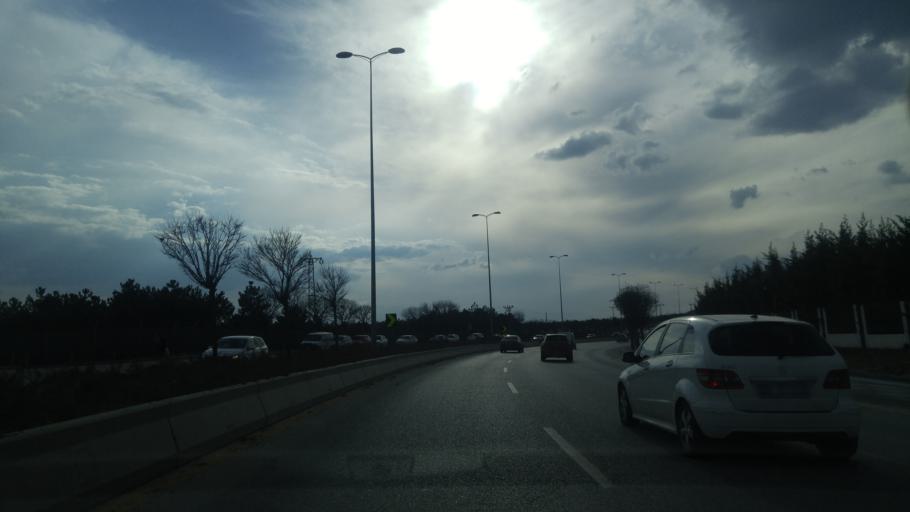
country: TR
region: Ankara
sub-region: Goelbasi
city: Golbasi
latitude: 39.8438
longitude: 32.7890
